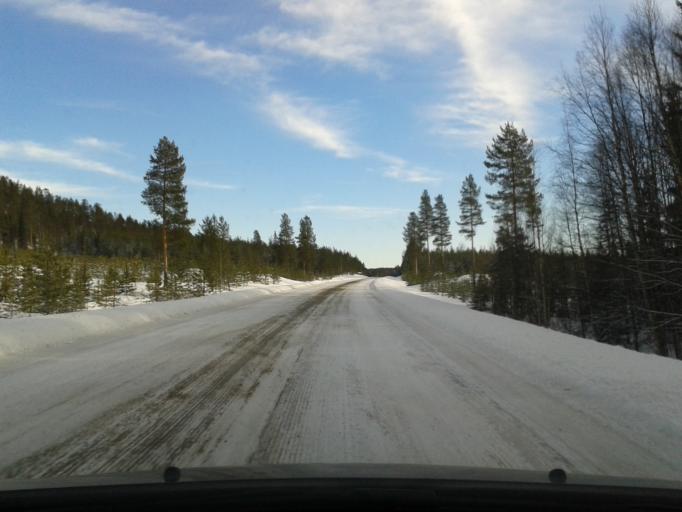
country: SE
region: Vaesterbotten
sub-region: Asele Kommun
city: Asele
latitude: 64.3107
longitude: 17.2336
